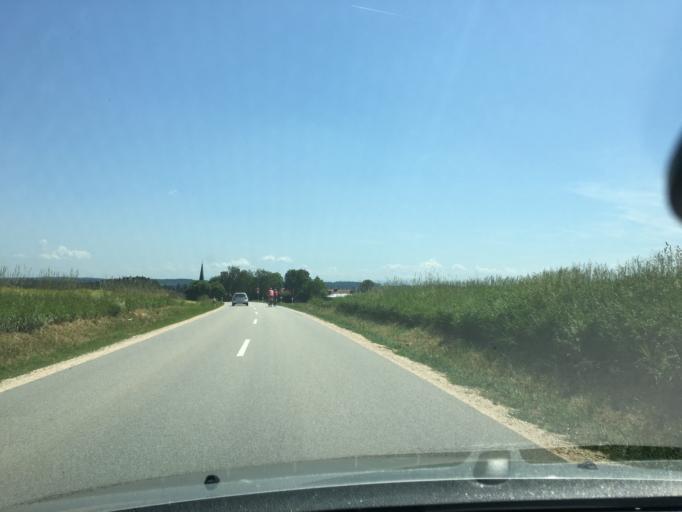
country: DE
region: Bavaria
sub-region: Upper Bavaria
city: Halsbach
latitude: 48.1277
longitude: 12.6684
